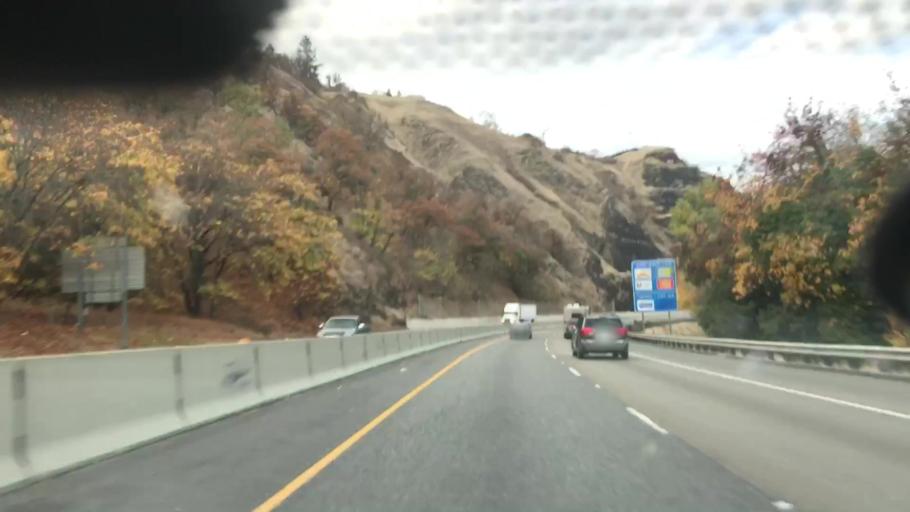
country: US
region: Oregon
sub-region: Douglas County
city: Roseburg
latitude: 43.2056
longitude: -123.3590
